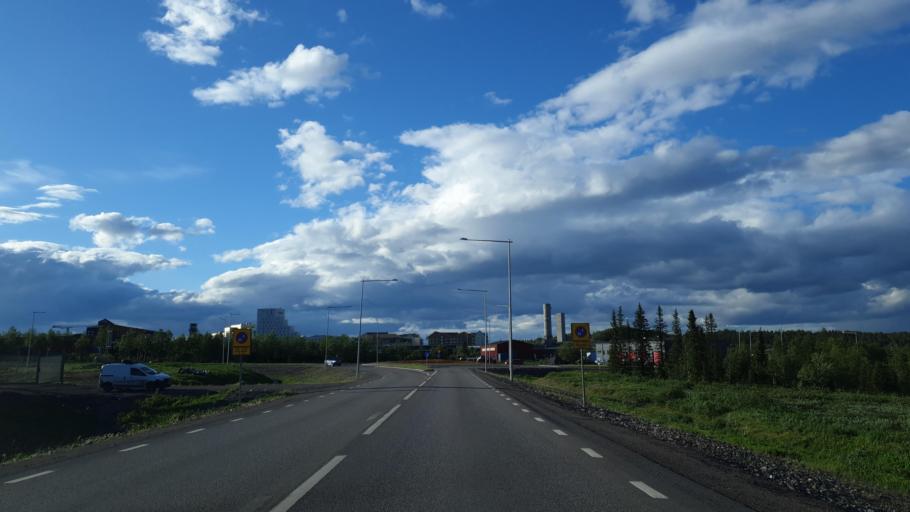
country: SE
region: Norrbotten
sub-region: Kiruna Kommun
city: Kiruna
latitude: 67.8423
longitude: 20.3085
